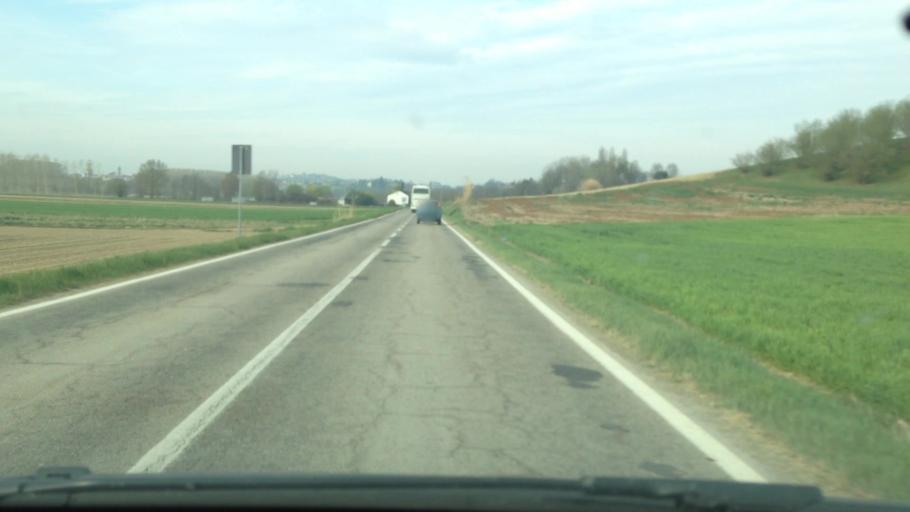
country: IT
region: Piedmont
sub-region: Provincia di Asti
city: San Damiano d'Asti
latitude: 44.8506
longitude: 8.0893
